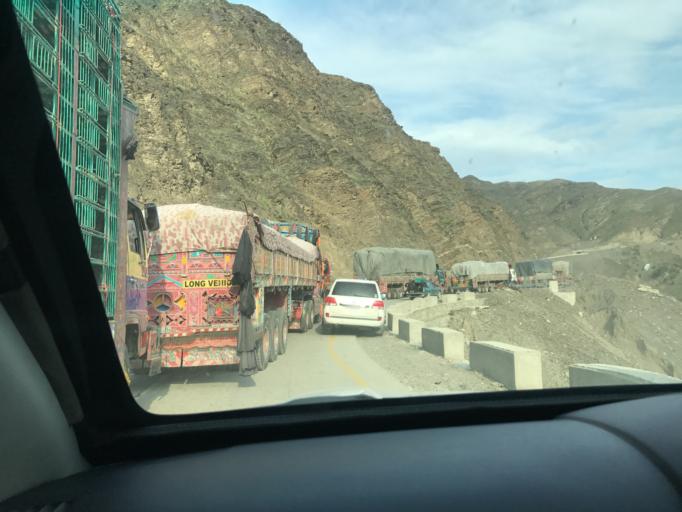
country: PK
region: Federally Administered Tribal Areas
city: Landi Kotal
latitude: 34.1110
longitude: 71.1134
